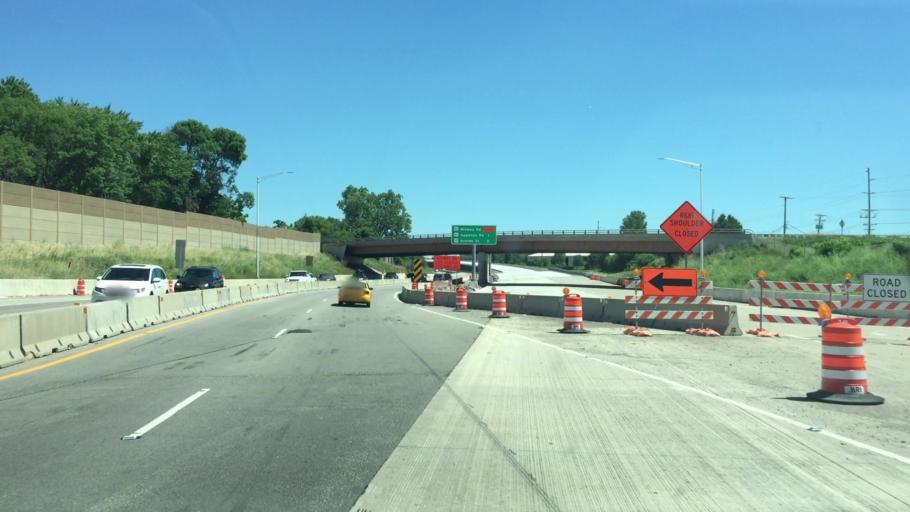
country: US
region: Wisconsin
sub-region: Winnebago County
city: Menasha
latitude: 44.2242
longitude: -88.4455
